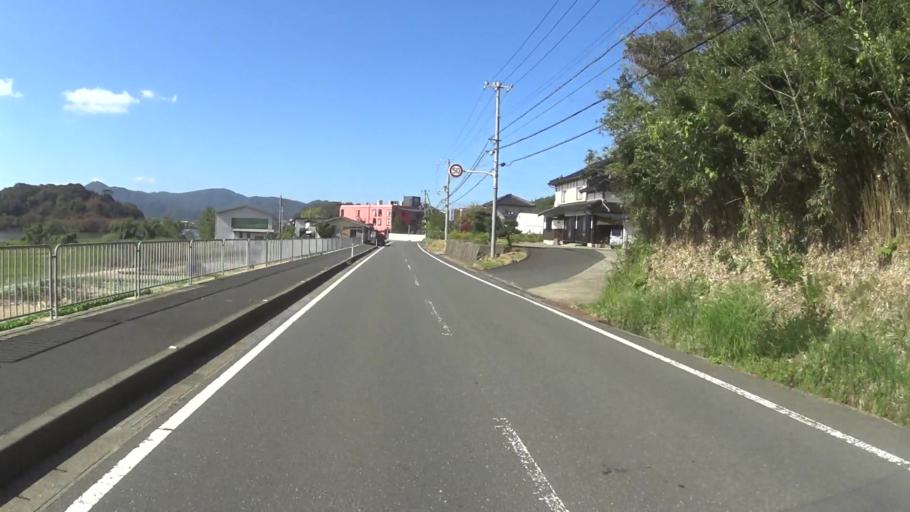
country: JP
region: Kyoto
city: Miyazu
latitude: 35.6932
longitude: 135.0451
